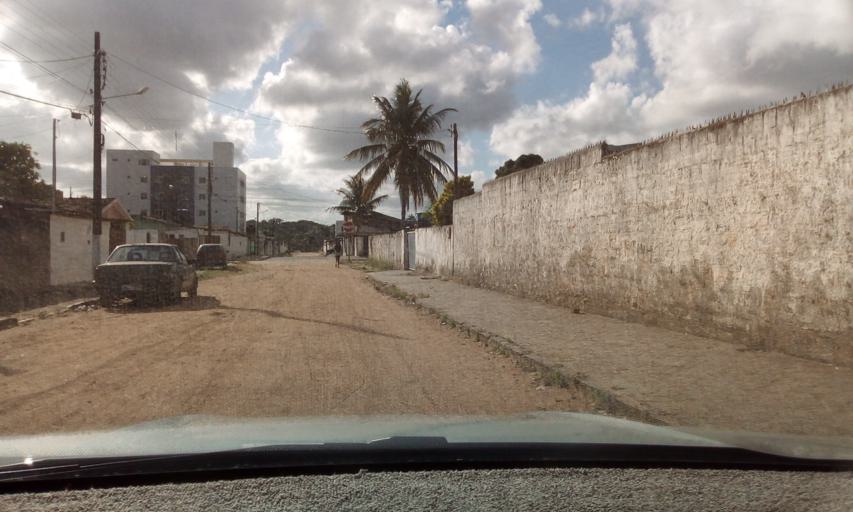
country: BR
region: Paraiba
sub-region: Bayeux
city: Bayeux
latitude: -7.1625
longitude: -34.9084
